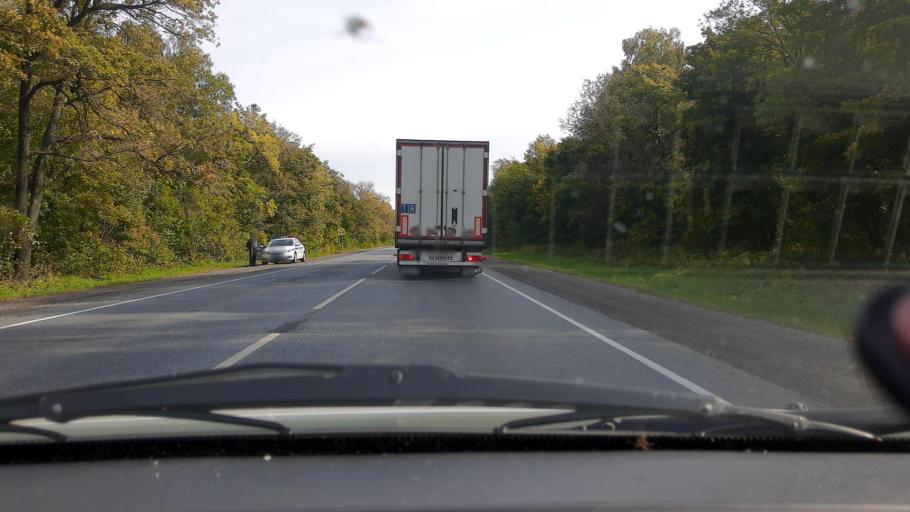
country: RU
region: Bashkortostan
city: Iglino
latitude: 54.7691
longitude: 56.4418
